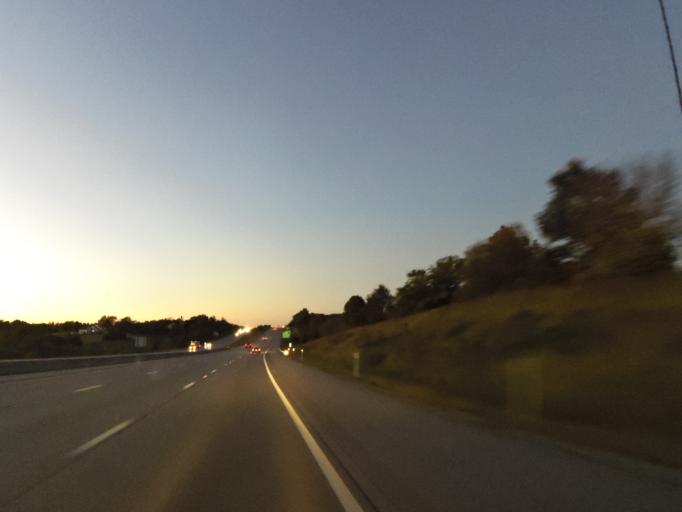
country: US
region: Kentucky
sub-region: Madison County
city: Richmond
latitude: 37.7037
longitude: -84.3183
